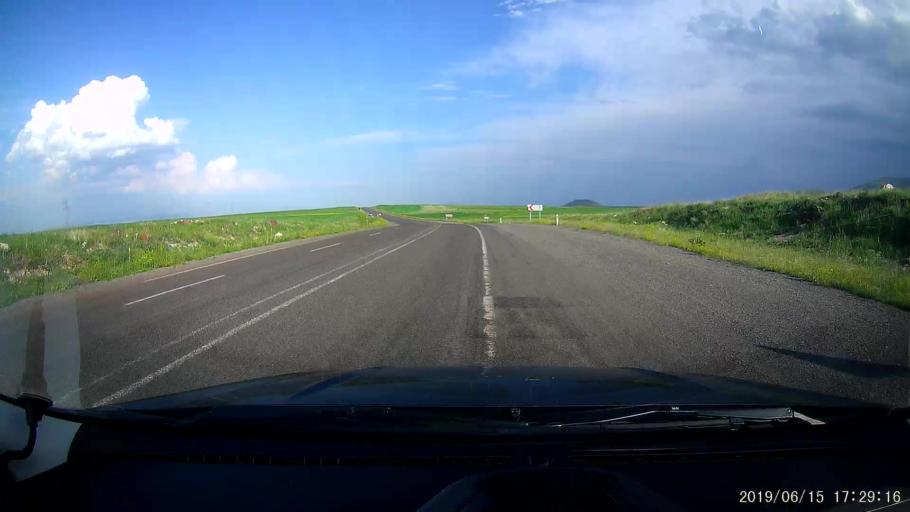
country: TR
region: Kars
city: Basgedikler
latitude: 40.5906
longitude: 43.4506
